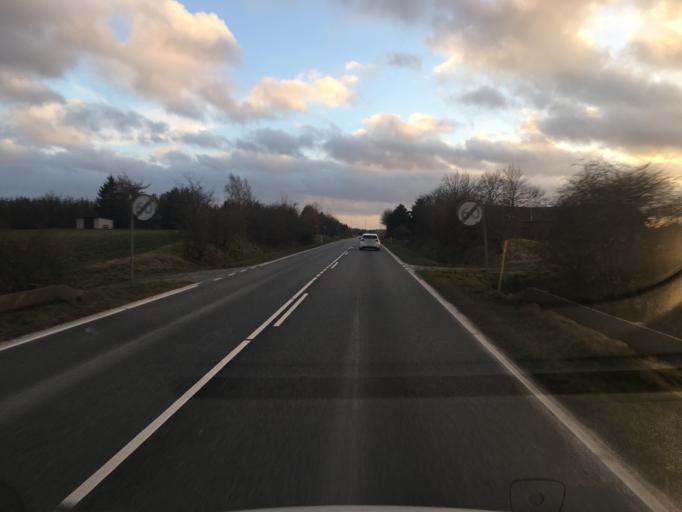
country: DK
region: South Denmark
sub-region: Aabenraa Kommune
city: Tinglev
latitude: 54.9531
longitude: 9.2796
